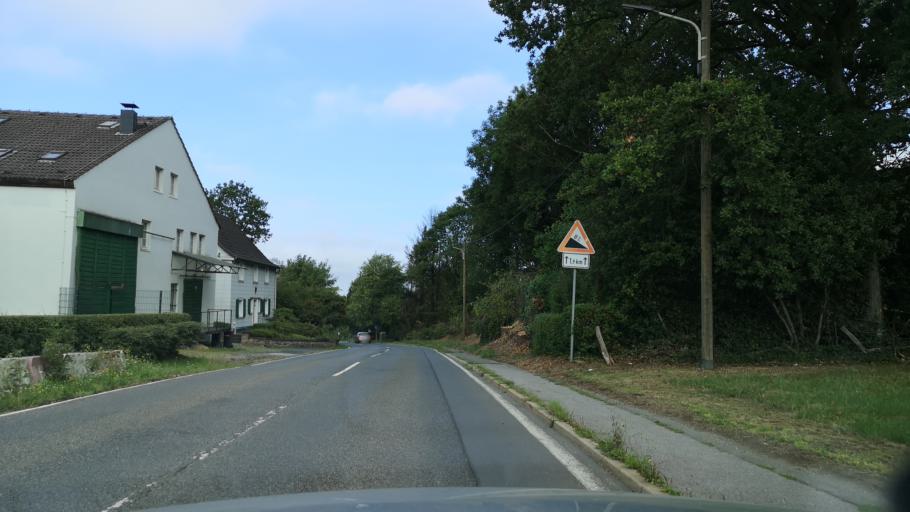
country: DE
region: North Rhine-Westphalia
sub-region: Regierungsbezirk Dusseldorf
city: Wuppertal
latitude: 51.3055
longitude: 7.1448
